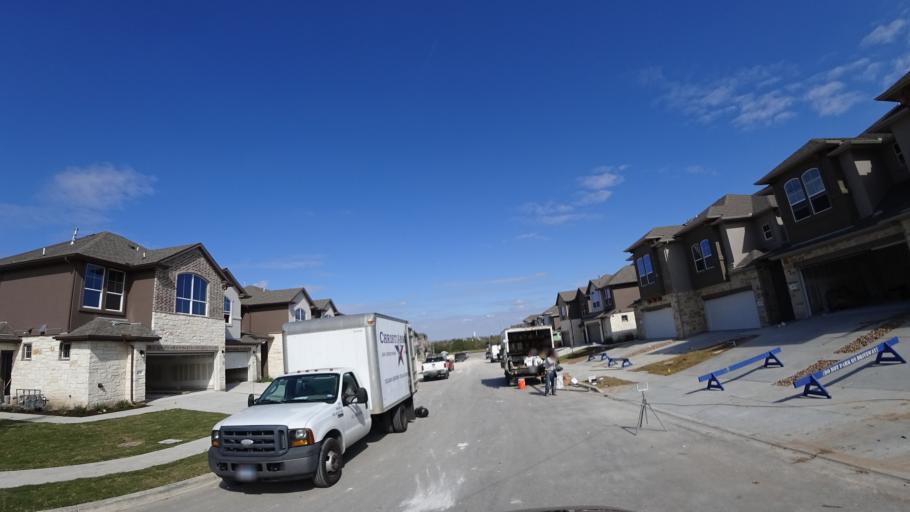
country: US
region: Texas
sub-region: Travis County
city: Windemere
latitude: 30.4499
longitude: -97.6359
